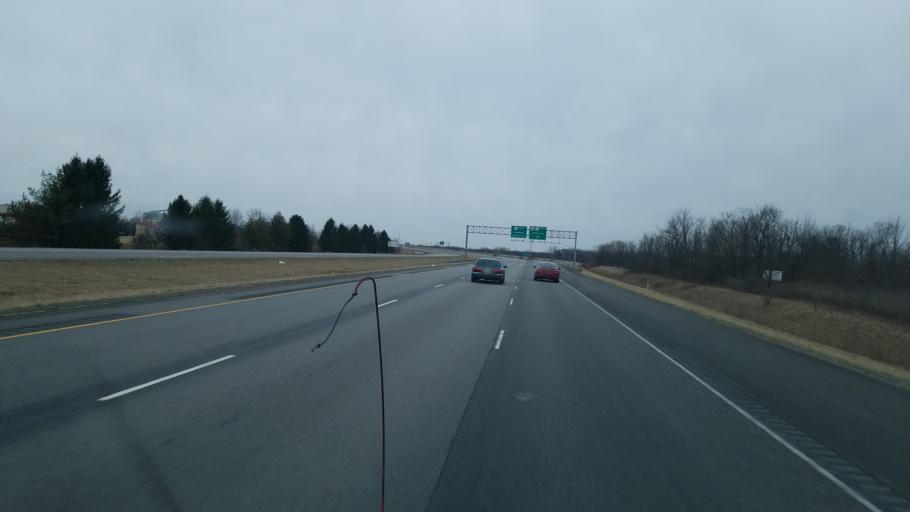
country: US
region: Indiana
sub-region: Porter County
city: Valparaiso
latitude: 41.4612
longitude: -87.0255
